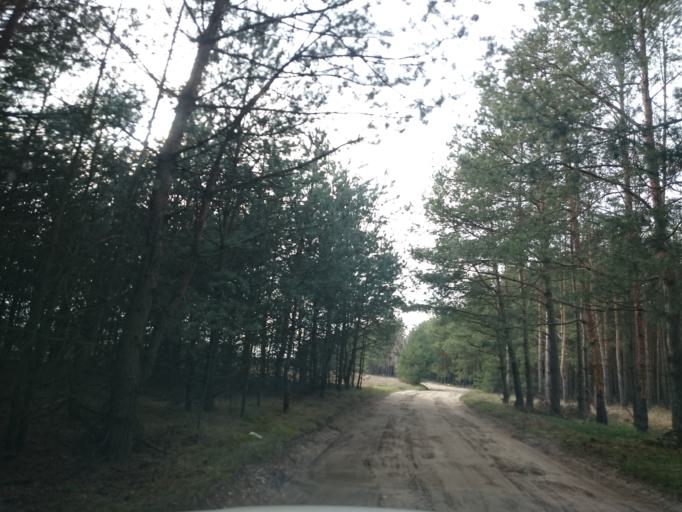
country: PL
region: Kujawsko-Pomorskie
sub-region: Powiat golubsko-dobrzynski
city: Ciechocin
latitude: 53.0499
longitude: 18.8604
